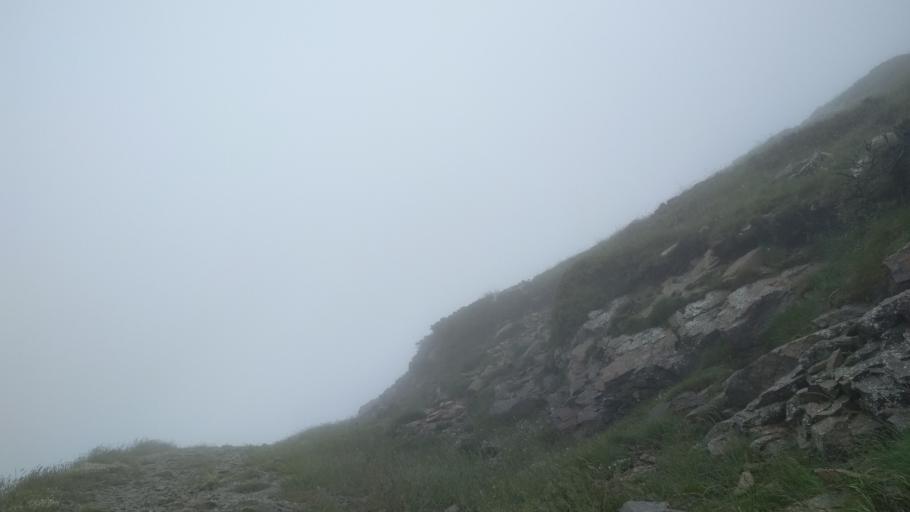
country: ES
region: Catalonia
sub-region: Provincia de Barcelona
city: Fogars de Montclus
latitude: 41.7767
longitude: 2.4344
